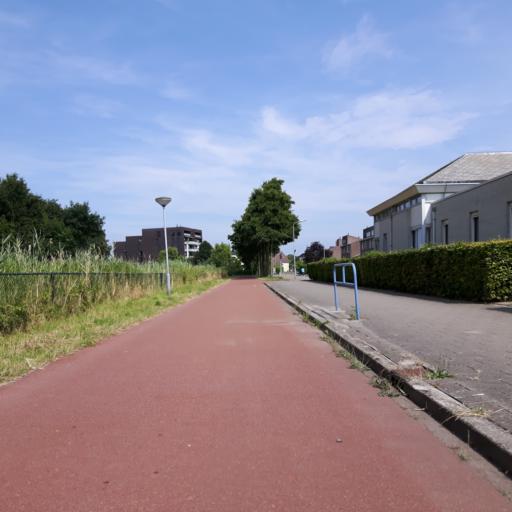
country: NL
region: Zeeland
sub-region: Gemeente Goes
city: Goes
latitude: 51.4906
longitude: 3.9009
